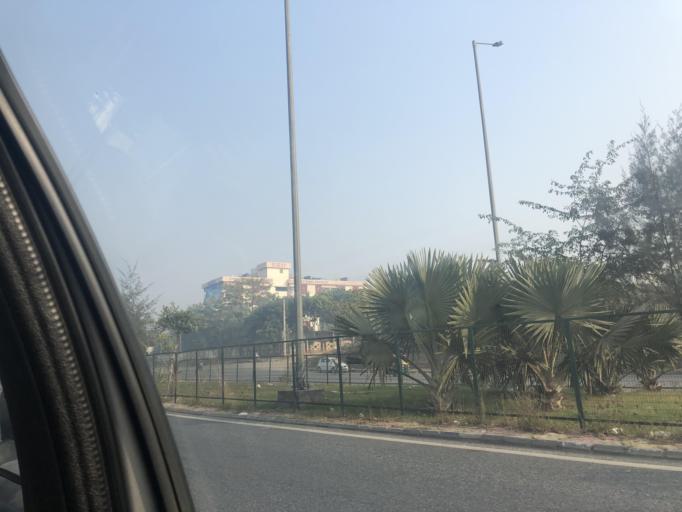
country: IN
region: NCT
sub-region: Central Delhi
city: Karol Bagh
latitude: 28.6140
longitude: 77.1364
